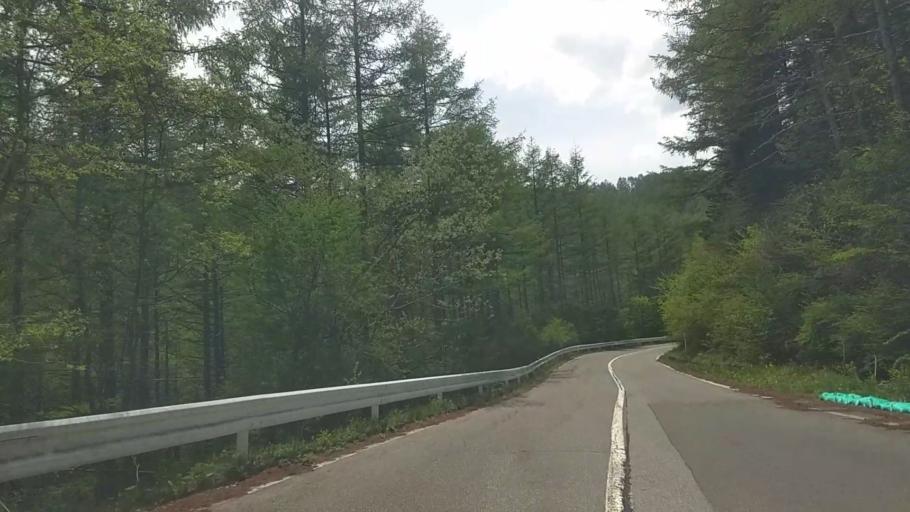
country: JP
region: Nagano
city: Saku
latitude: 36.0929
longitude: 138.3874
